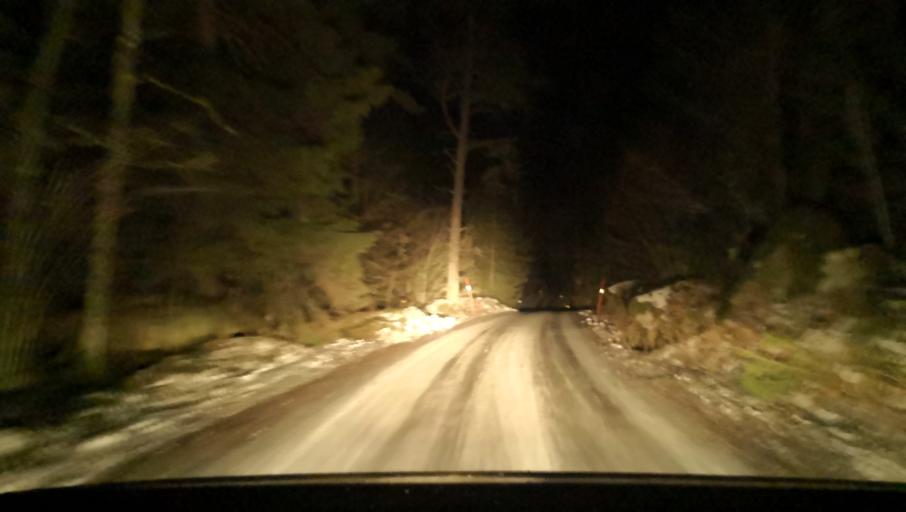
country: SE
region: Uppsala
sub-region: Enkopings Kommun
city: Hummelsta
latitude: 59.6333
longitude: 16.8761
